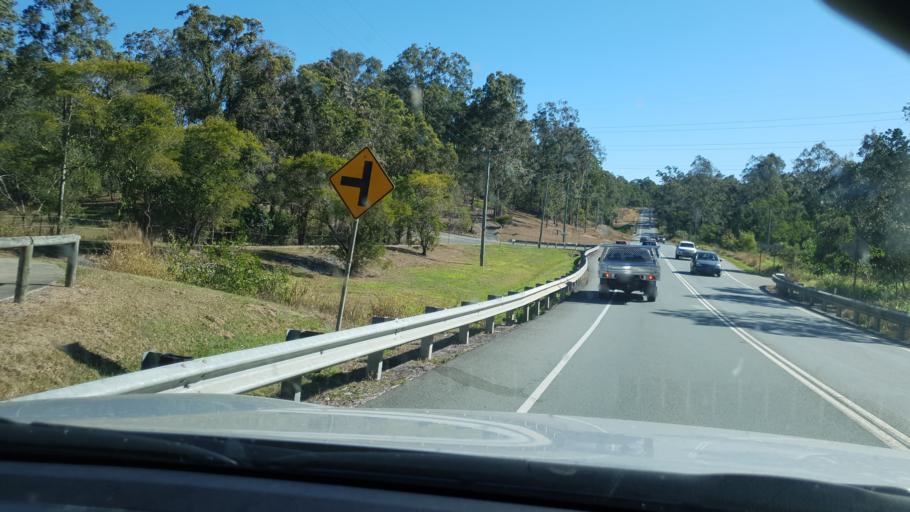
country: AU
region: Queensland
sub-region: Moreton Bay
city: Strathpine
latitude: -27.3294
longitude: 152.9437
